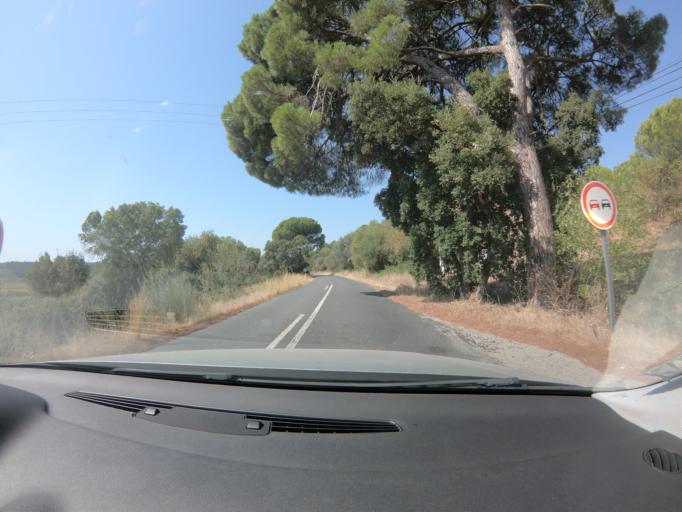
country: PT
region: Setubal
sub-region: Alcacer do Sal
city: Alcacer do Sal
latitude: 38.2793
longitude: -8.3859
